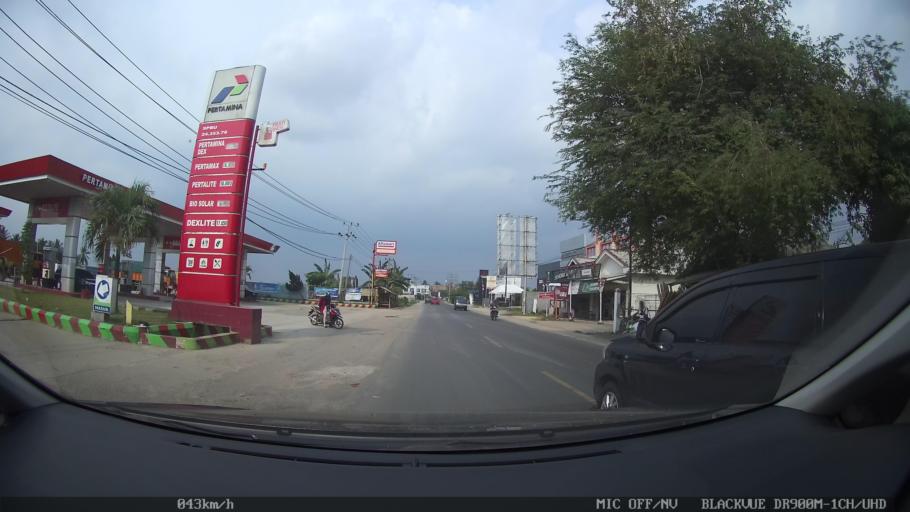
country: ID
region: Lampung
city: Gadingrejo
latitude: -5.3811
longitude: 105.0243
